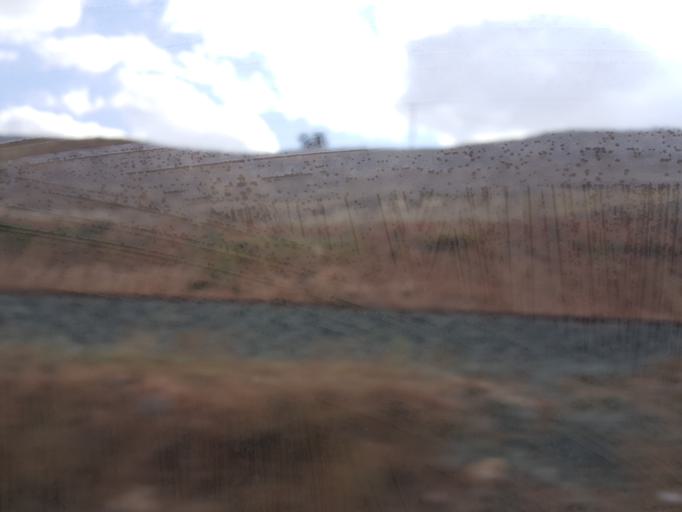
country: TR
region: Tokat
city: Yesilyurt
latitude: 40.0154
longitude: 36.2415
